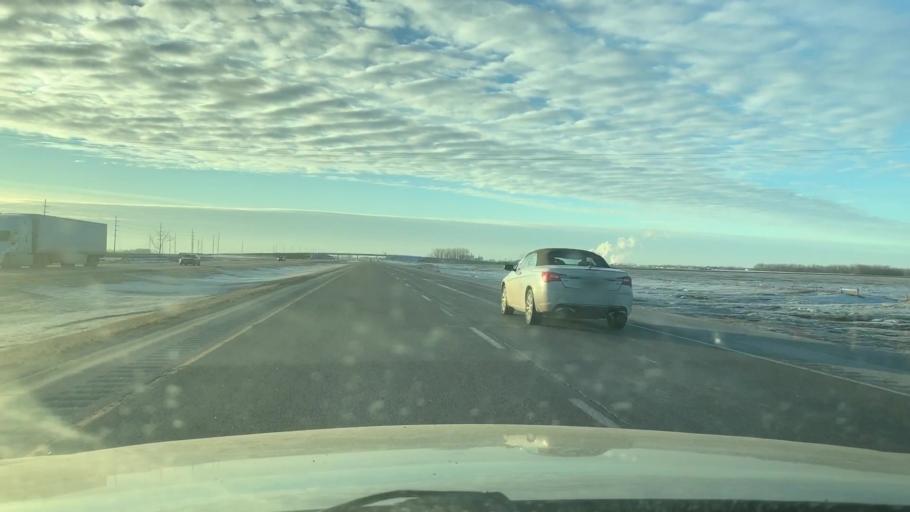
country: US
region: North Dakota
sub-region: Cass County
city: Casselton
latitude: 46.8768
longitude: -97.1476
